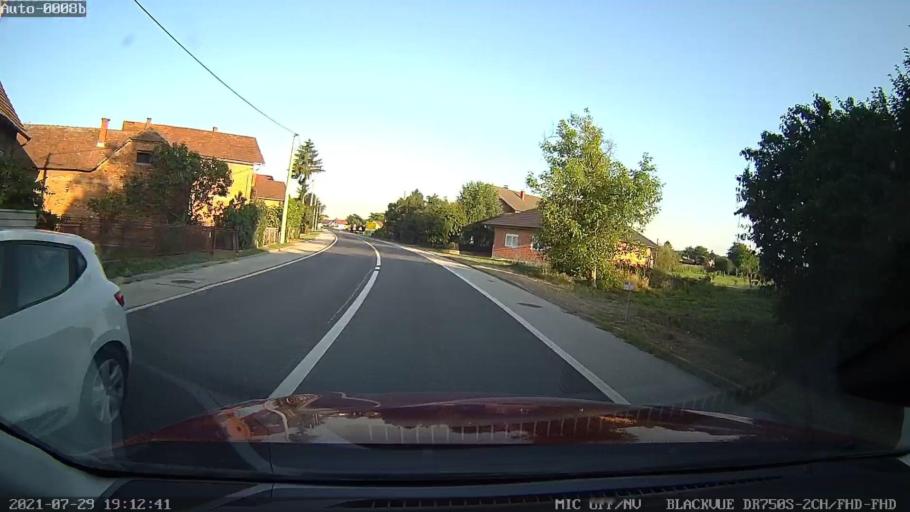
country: HR
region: Varazdinska
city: Jalzabet
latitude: 46.2655
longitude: 16.5178
